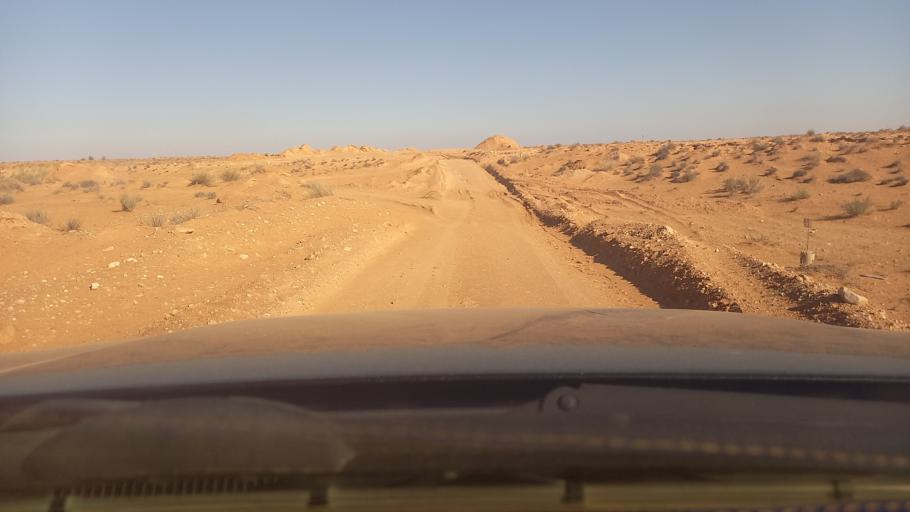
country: TN
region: Madanin
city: Medenine
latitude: 33.1486
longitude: 10.5078
